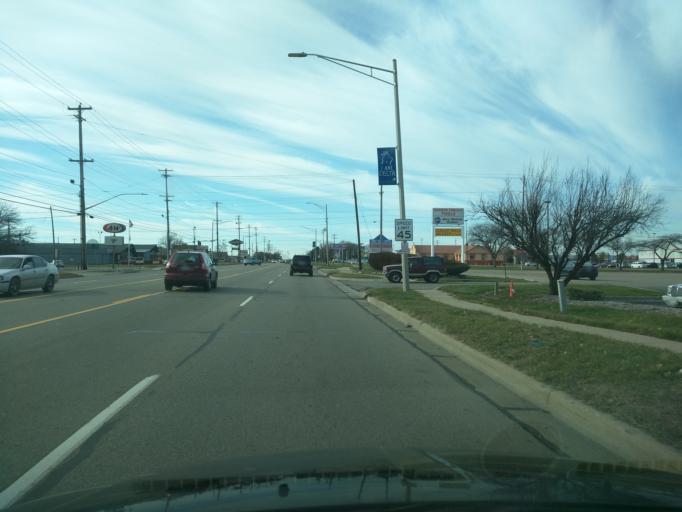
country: US
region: Michigan
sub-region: Eaton County
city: Waverly
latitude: 42.7410
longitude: -84.6180
